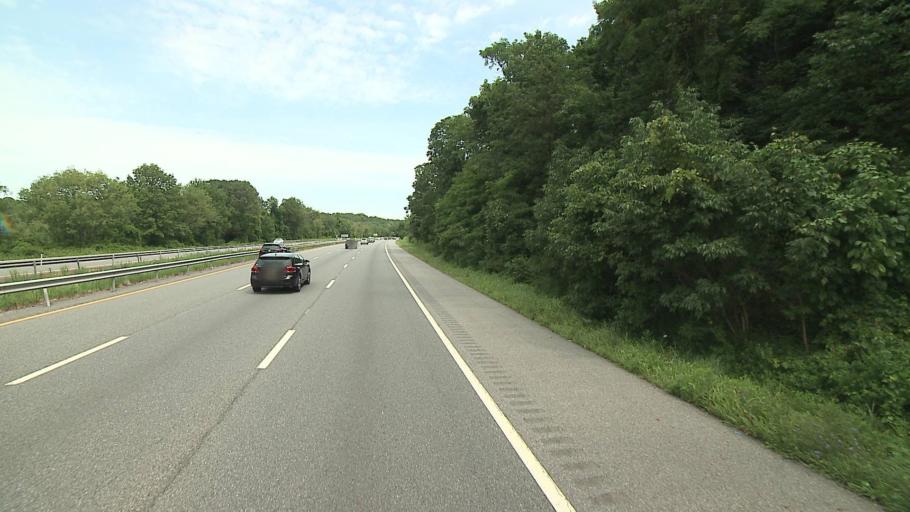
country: US
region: New York
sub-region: Westchester County
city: Armonk
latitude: 41.0898
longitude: -73.7178
